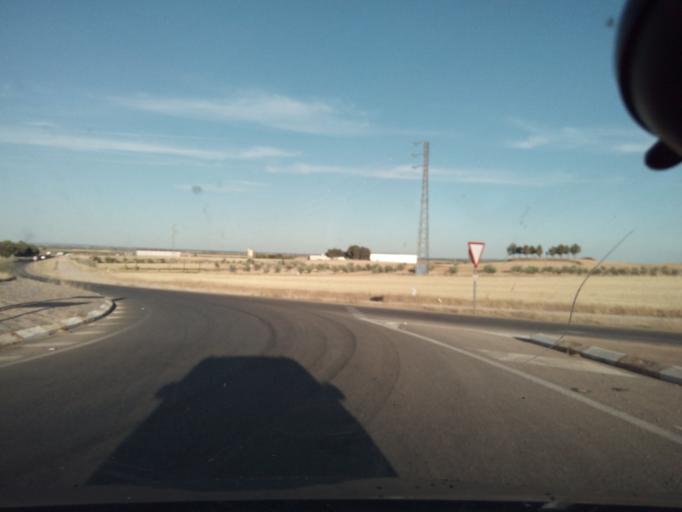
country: ES
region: Castille-La Mancha
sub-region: Province of Toledo
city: Villacanas
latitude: 39.6100
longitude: -3.3472
